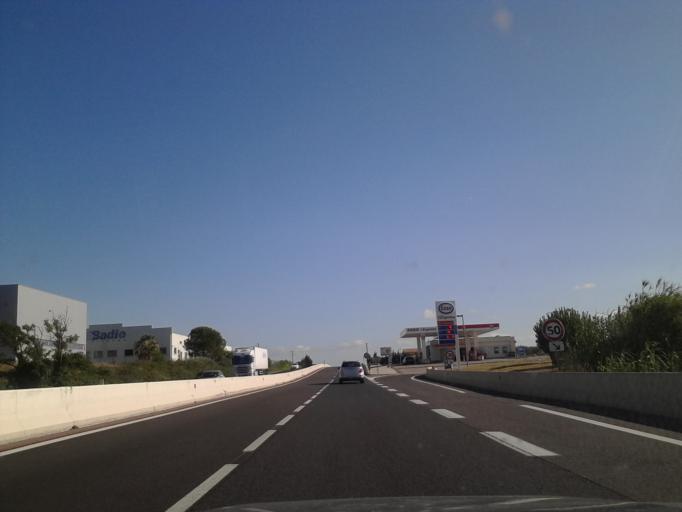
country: FR
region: Languedoc-Roussillon
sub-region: Departement des Pyrenees-Orientales
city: Pia
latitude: 42.7478
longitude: 2.8942
